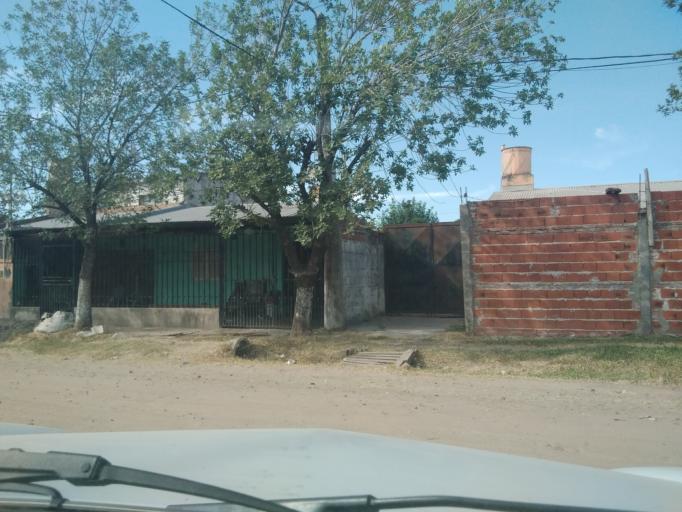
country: AR
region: Corrientes
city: Corrientes
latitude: -27.5093
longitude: -58.8006
